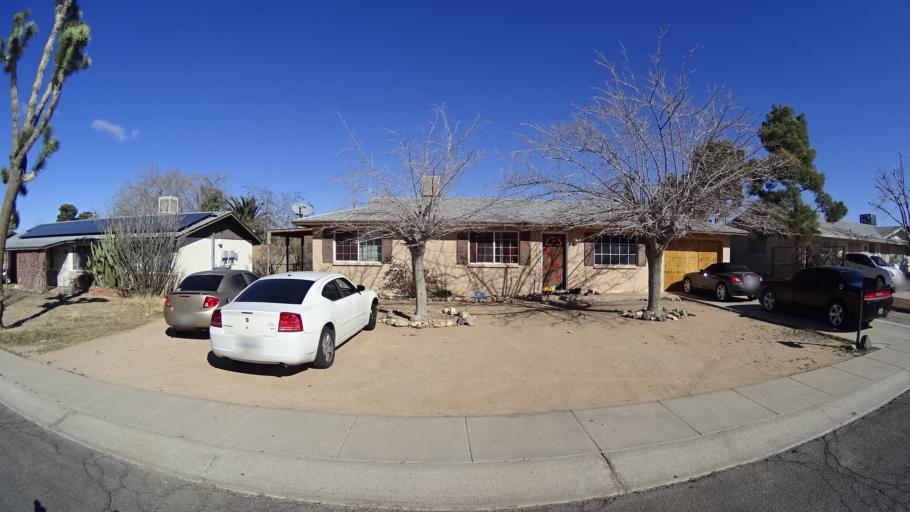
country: US
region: Arizona
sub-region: Mohave County
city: Kingman
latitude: 35.1949
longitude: -114.0189
